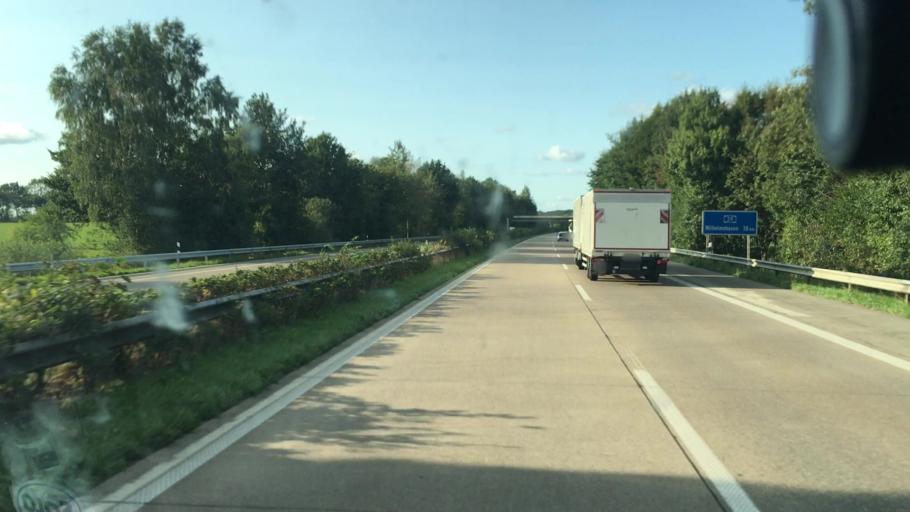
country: DE
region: Lower Saxony
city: Wiefelstede
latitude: 53.2862
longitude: 8.1510
